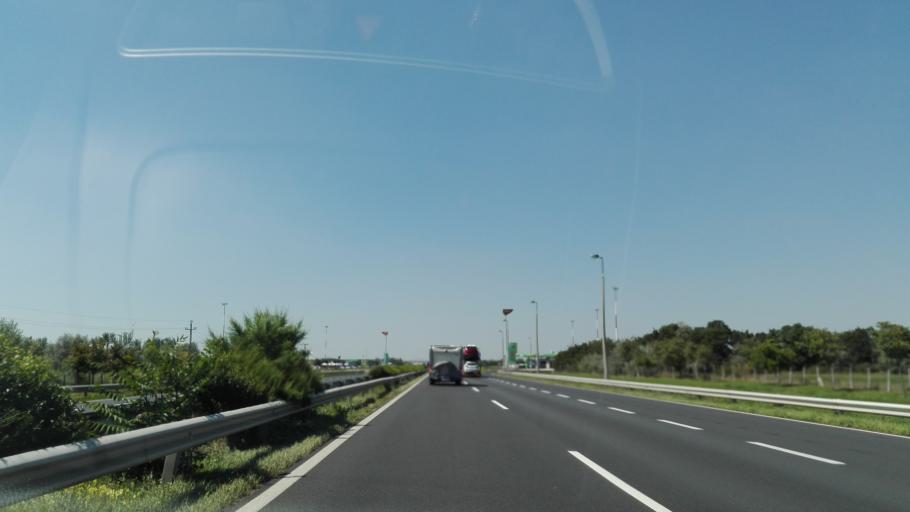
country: HU
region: Gyor-Moson-Sopron
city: Mosonmagyarovar
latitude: 47.8691
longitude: 17.2206
